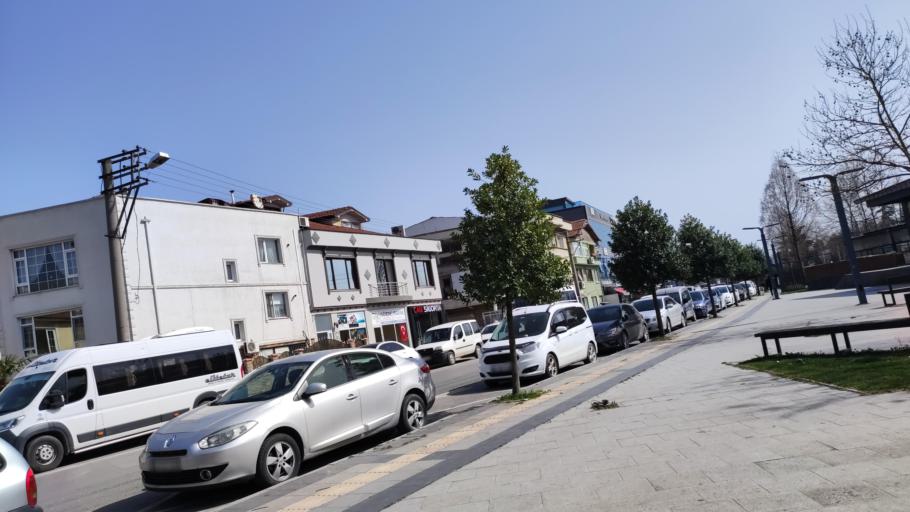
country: TR
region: Sakarya
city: Adapazari
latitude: 40.7730
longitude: 30.3925
